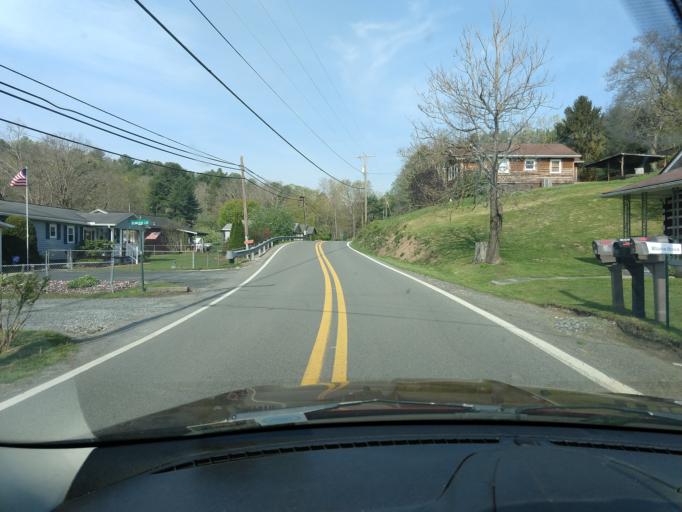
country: US
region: West Virginia
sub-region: Raleigh County
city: Crab Orchard
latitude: 37.7414
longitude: -81.2406
